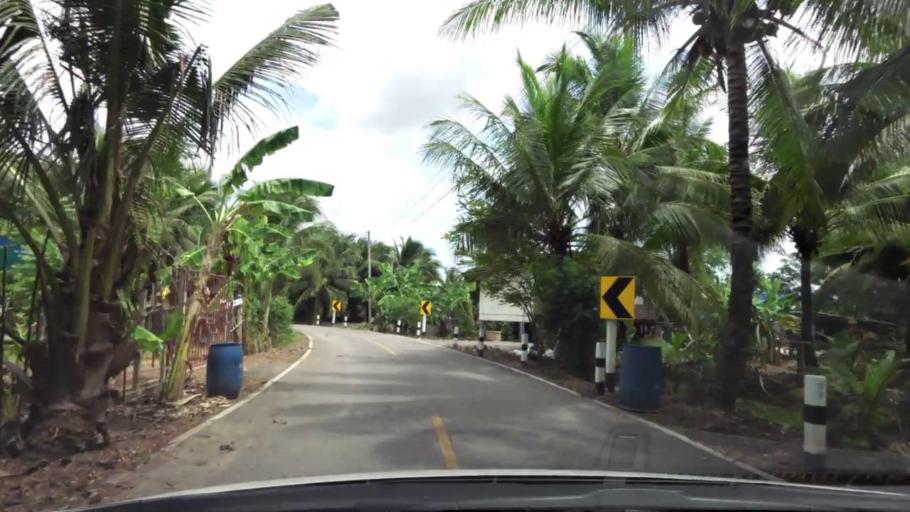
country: TH
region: Ratchaburi
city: Damnoen Saduak
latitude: 13.5103
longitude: 100.0144
